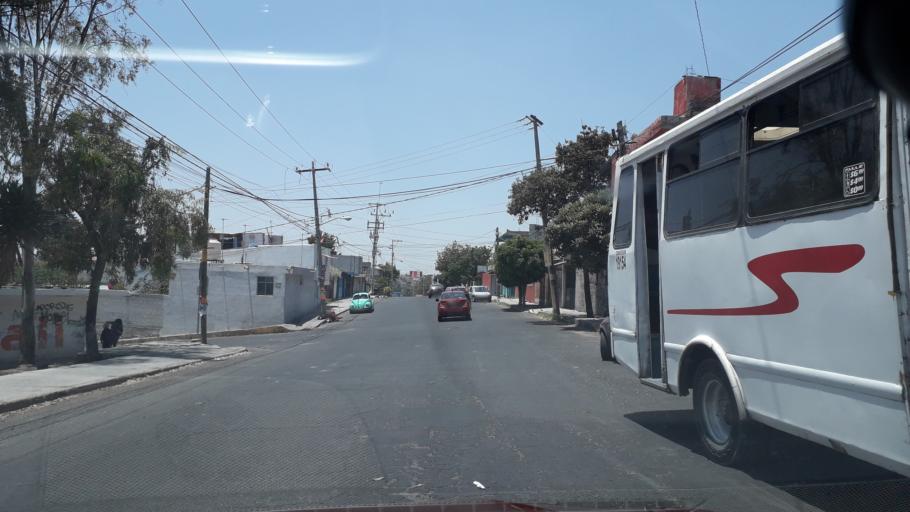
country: MX
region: Puebla
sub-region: Puebla
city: Galaxia la Calera
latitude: 18.9971
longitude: -98.1826
